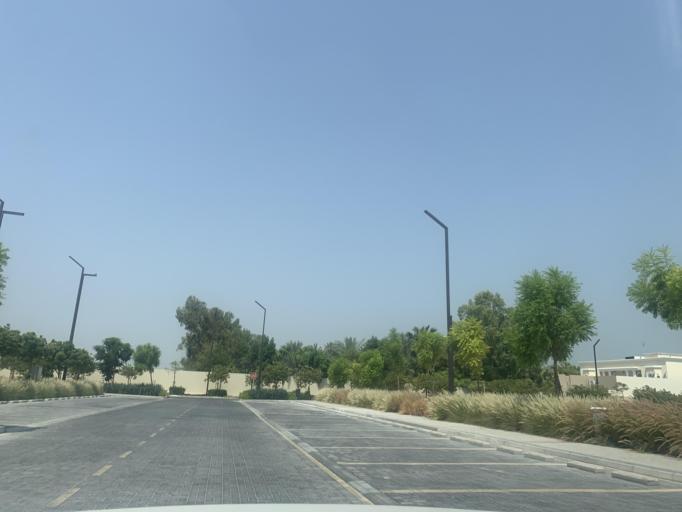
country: BH
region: Central Governorate
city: Madinat Hamad
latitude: 26.1633
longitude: 50.4690
